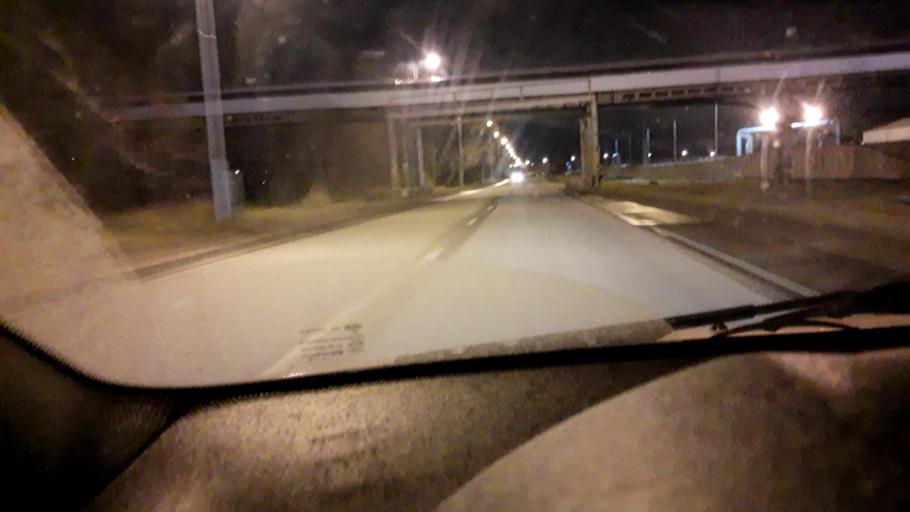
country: RU
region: Bashkortostan
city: Blagoveshchensk
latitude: 54.9149
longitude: 56.0653
